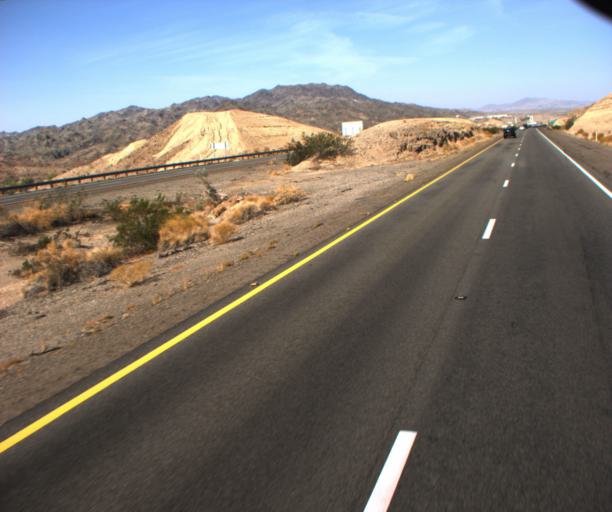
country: US
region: Arizona
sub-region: Mohave County
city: Desert Hills
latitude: 34.7193
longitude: -114.4606
